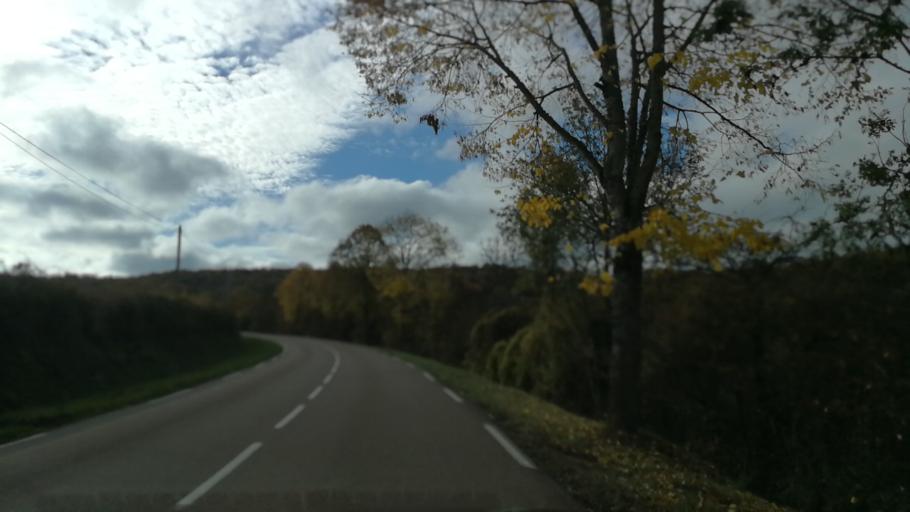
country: FR
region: Bourgogne
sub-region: Departement de la Cote-d'Or
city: Pouilly-en-Auxois
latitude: 47.2671
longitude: 4.4752
